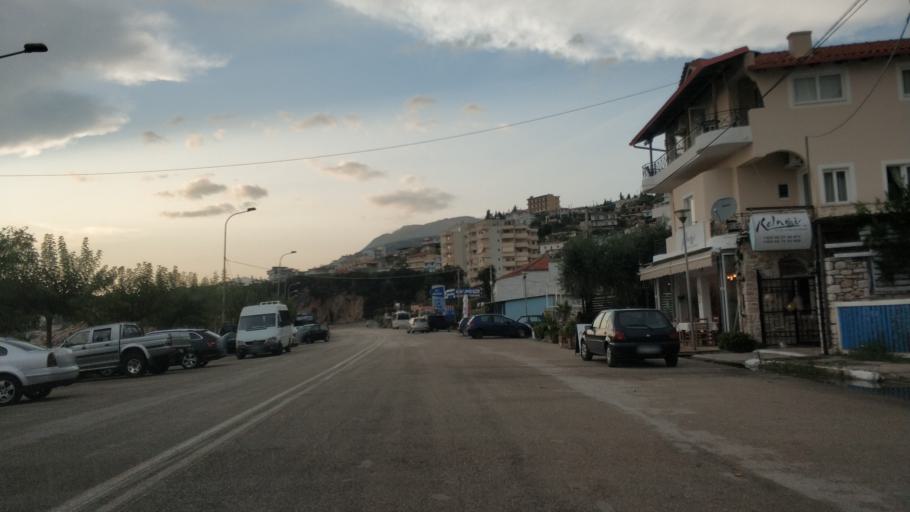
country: AL
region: Vlore
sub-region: Rrethi i Vlores
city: Himare
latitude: 40.0977
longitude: 19.7532
